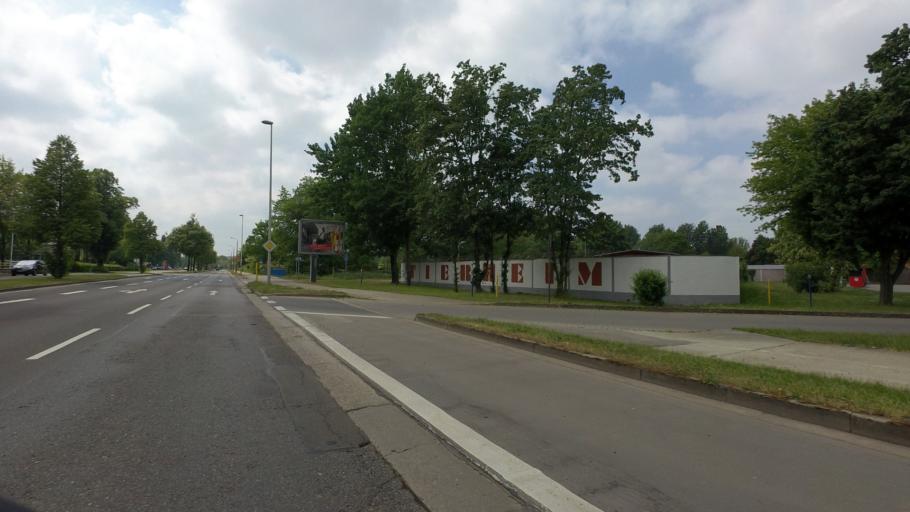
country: DE
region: Brandenburg
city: Cottbus
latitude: 51.7725
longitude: 14.3608
